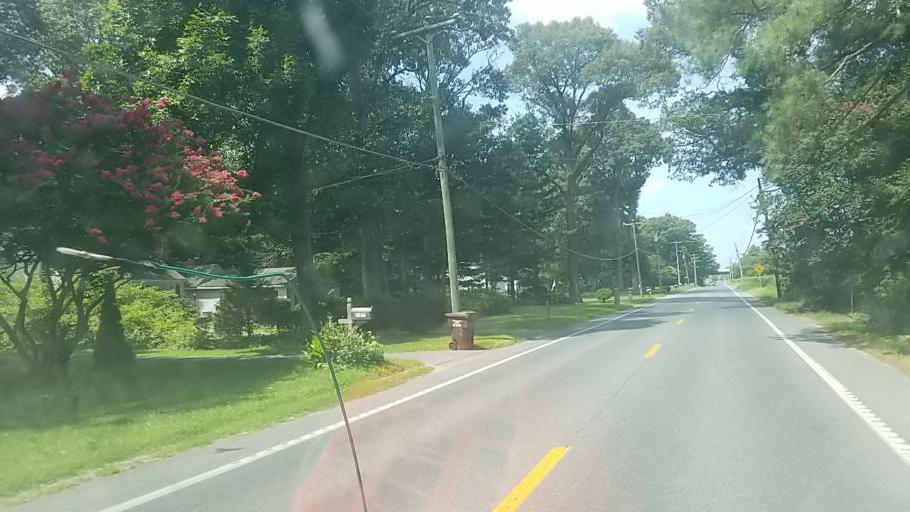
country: US
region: Maryland
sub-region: Wicomico County
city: Salisbury
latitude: 38.3561
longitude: -75.5357
